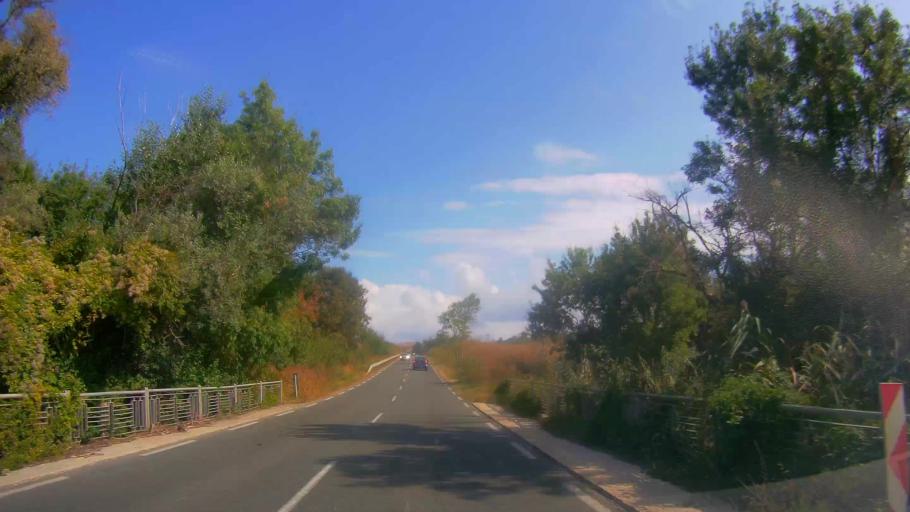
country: BG
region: Burgas
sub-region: Obshtina Burgas
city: Burgas
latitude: 42.4758
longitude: 27.3575
